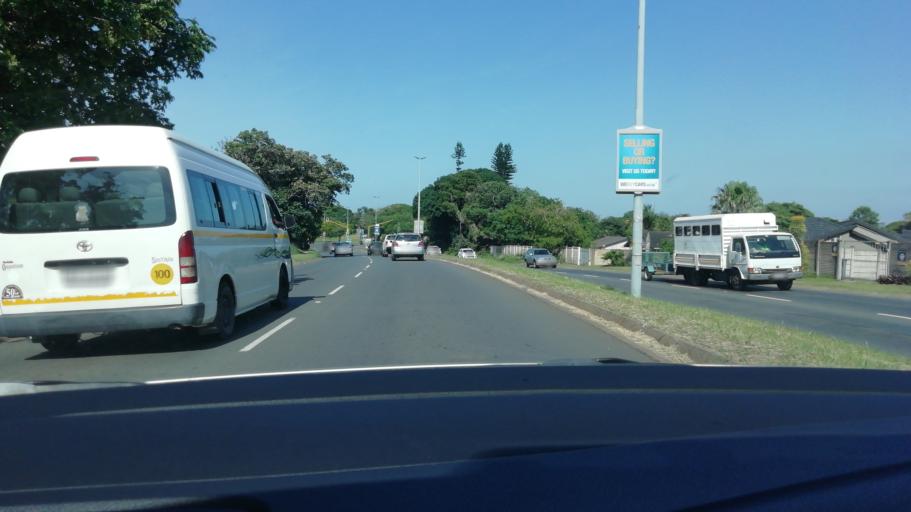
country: ZA
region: KwaZulu-Natal
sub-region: uThungulu District Municipality
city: Richards Bay
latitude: -28.7827
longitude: 32.0991
